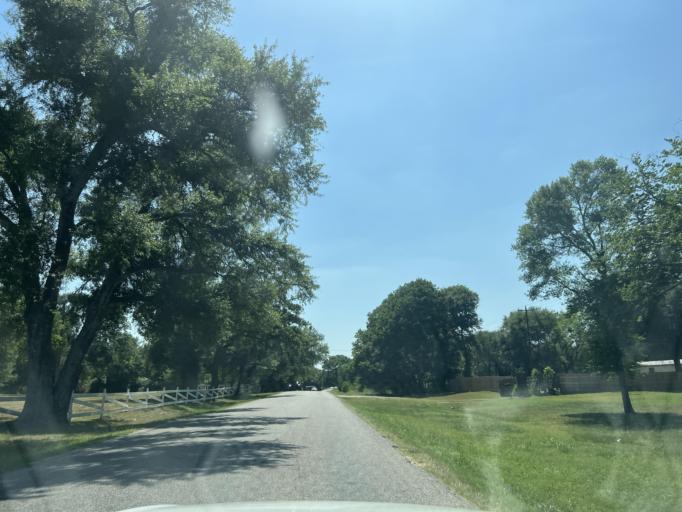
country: US
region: Texas
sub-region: Washington County
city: Brenham
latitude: 30.1618
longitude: -96.4263
